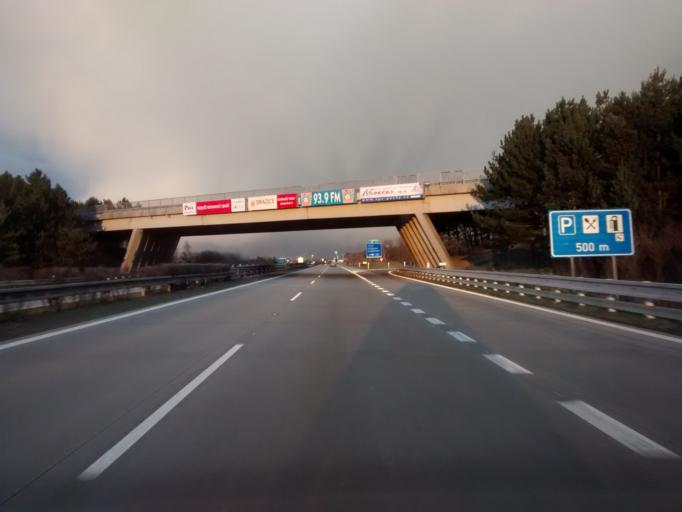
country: CZ
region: Central Bohemia
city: Cerhenice
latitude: 50.1209
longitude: 15.0697
